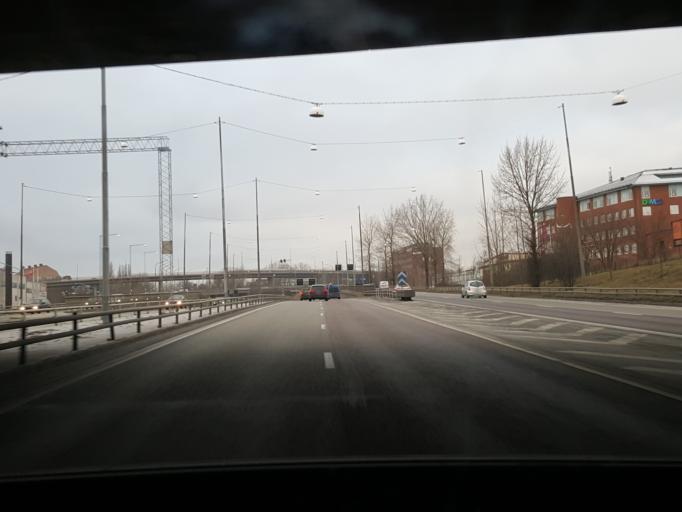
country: SE
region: Stockholm
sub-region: Stockholms Kommun
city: Arsta
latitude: 59.2992
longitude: 18.0272
